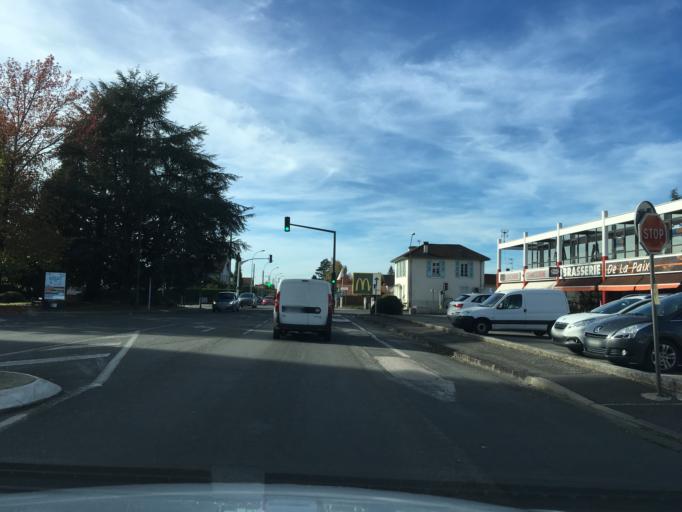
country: FR
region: Aquitaine
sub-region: Departement des Pyrenees-Atlantiques
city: Pau
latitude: 43.3227
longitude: -0.3690
